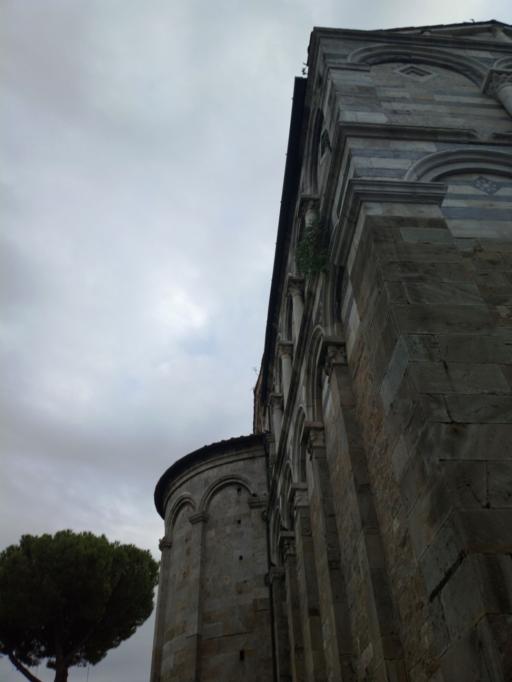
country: IT
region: Tuscany
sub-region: Province of Pisa
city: Pisa
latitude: 43.7131
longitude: 10.3938
